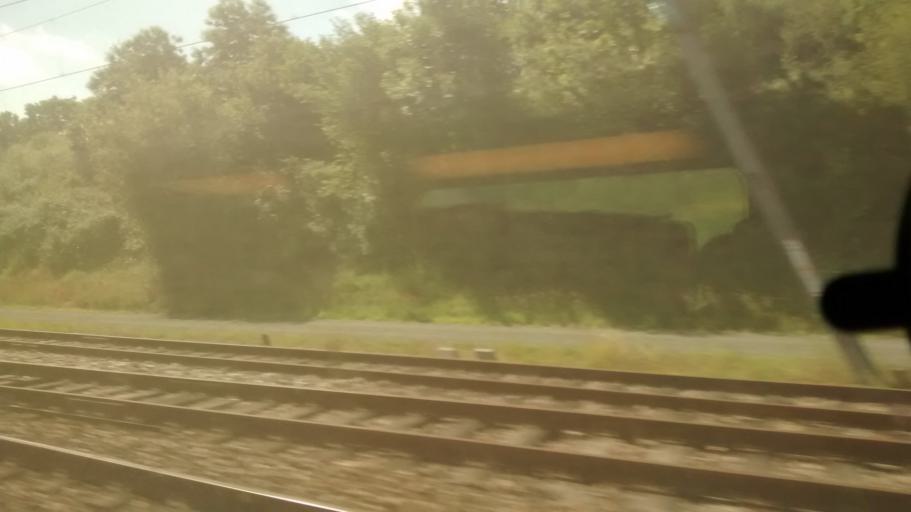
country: FR
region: Centre
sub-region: Departement du Loir-et-Cher
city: Mondoubleau
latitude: 48.0851
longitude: 0.8706
